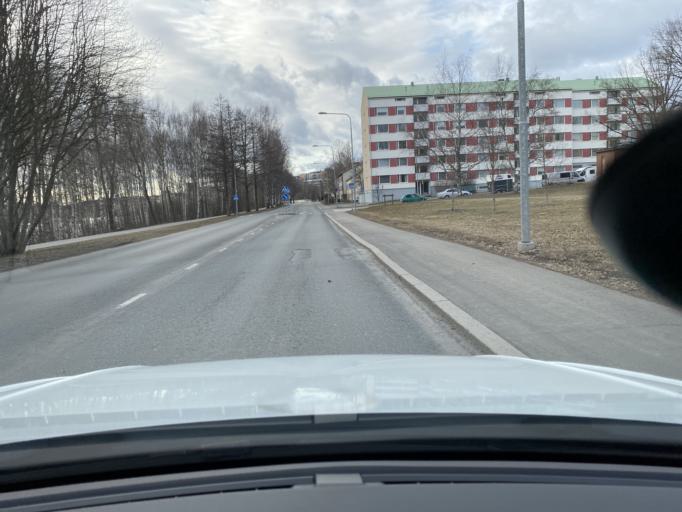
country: FI
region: Pirkanmaa
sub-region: Tampere
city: Tampere
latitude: 61.4886
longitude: 23.8022
